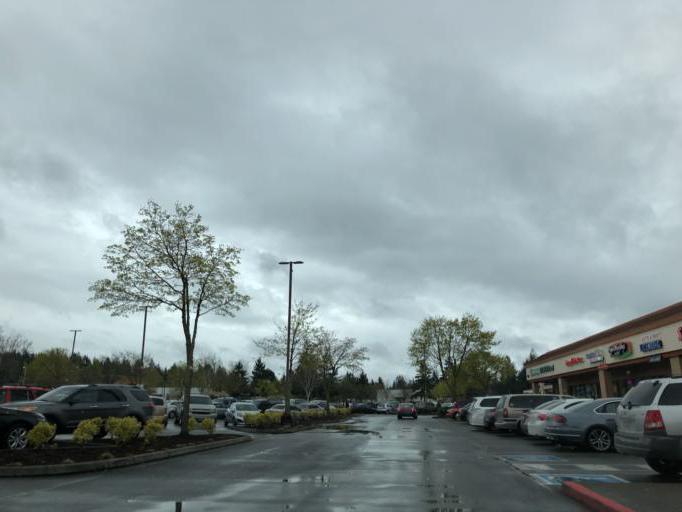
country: US
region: Washington
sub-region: Thurston County
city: Tanglewilde-Thompson Place
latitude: 47.0595
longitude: -122.7662
